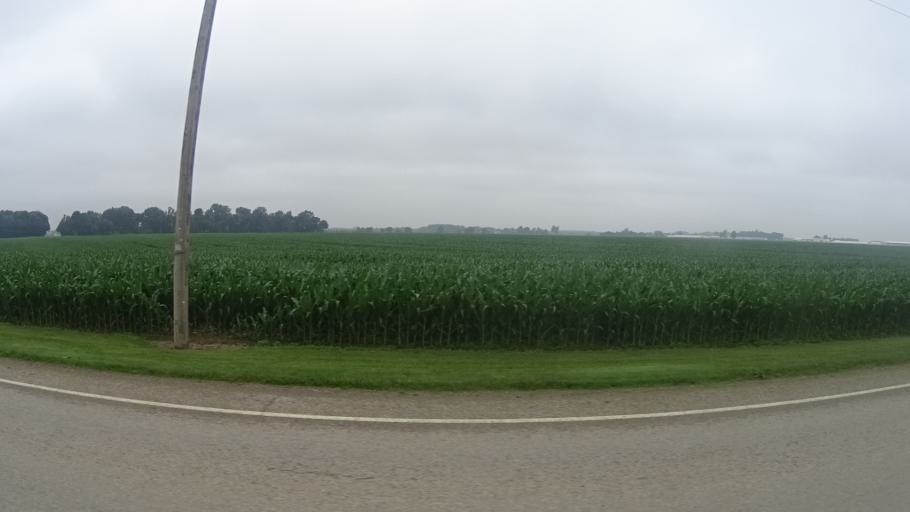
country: US
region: Ohio
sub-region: Erie County
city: Milan
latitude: 41.3456
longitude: -82.6119
